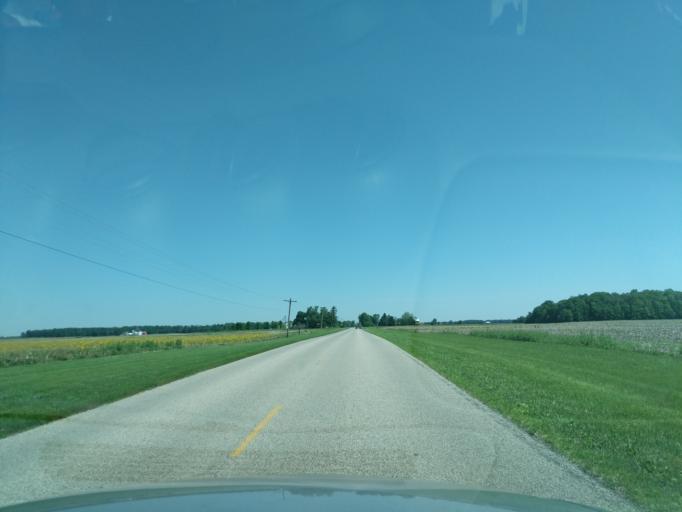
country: US
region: Indiana
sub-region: Huntington County
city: Huntington
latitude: 40.7877
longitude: -85.5077
